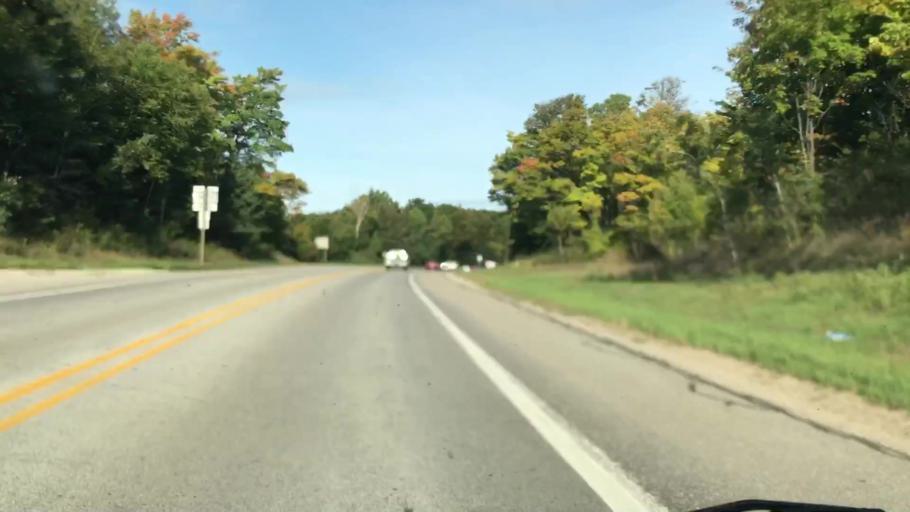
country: US
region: Michigan
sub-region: Luce County
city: Newberry
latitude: 46.3040
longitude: -85.5144
